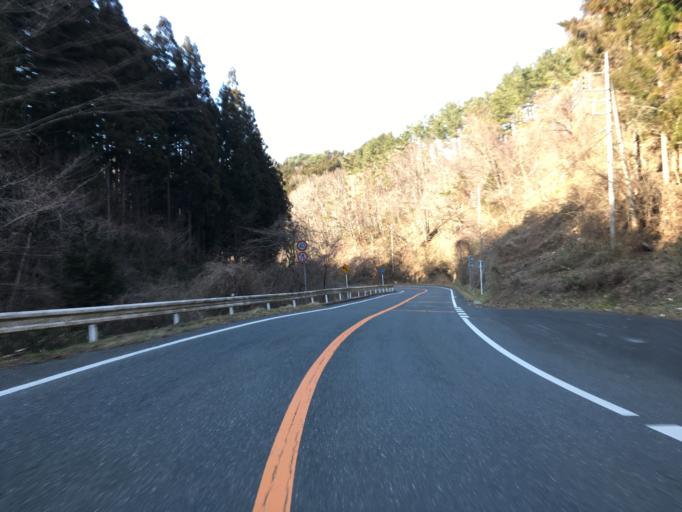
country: JP
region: Ibaraki
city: Hitachi
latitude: 36.7370
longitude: 140.5404
